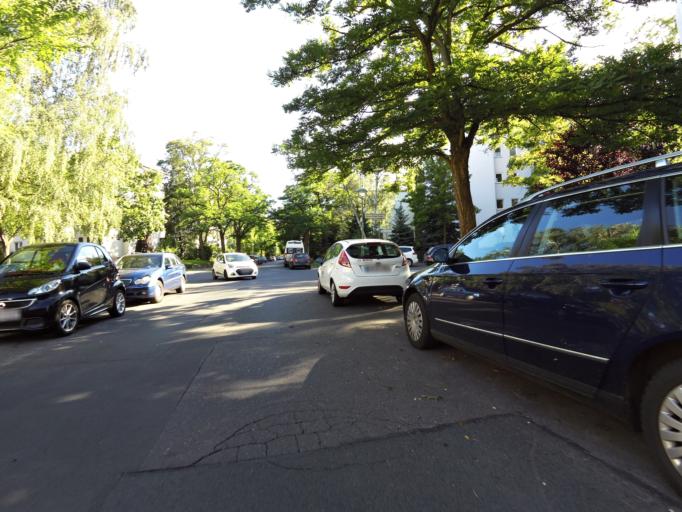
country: DE
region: Berlin
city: Steglitz Bezirk
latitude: 52.4471
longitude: 13.3318
